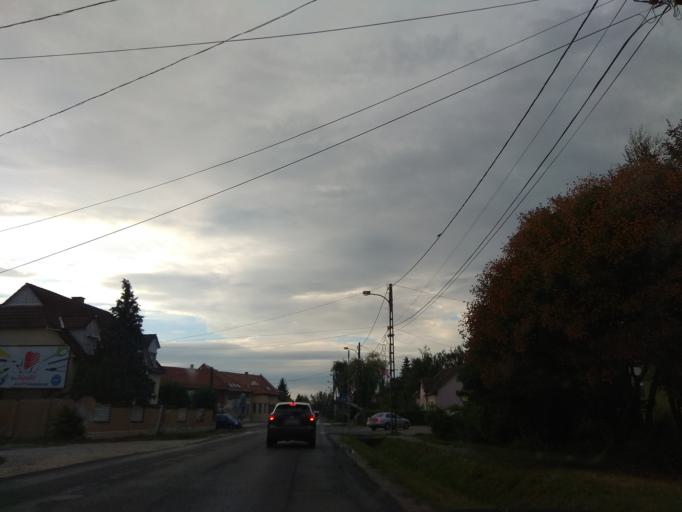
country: HU
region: Borsod-Abauj-Zemplen
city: Miskolc
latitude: 48.0916
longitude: 20.8073
